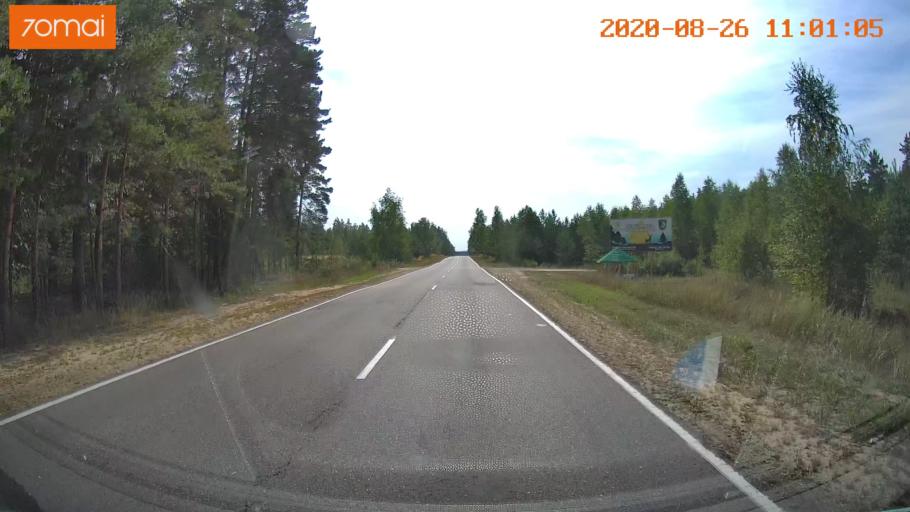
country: RU
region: Rjazan
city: Izhevskoye
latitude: 54.5673
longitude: 41.2204
